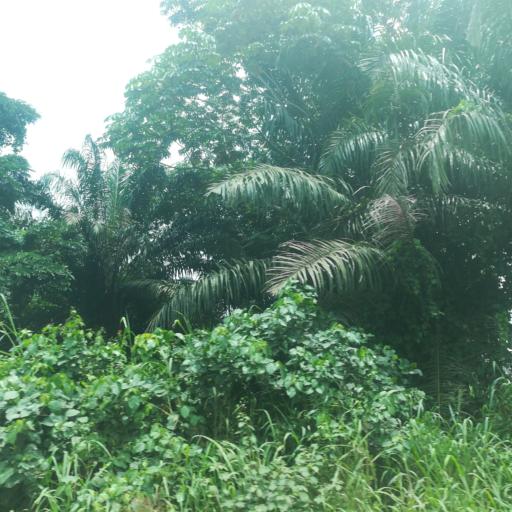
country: NG
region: Lagos
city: Ejirin
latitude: 6.6817
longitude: 3.7990
